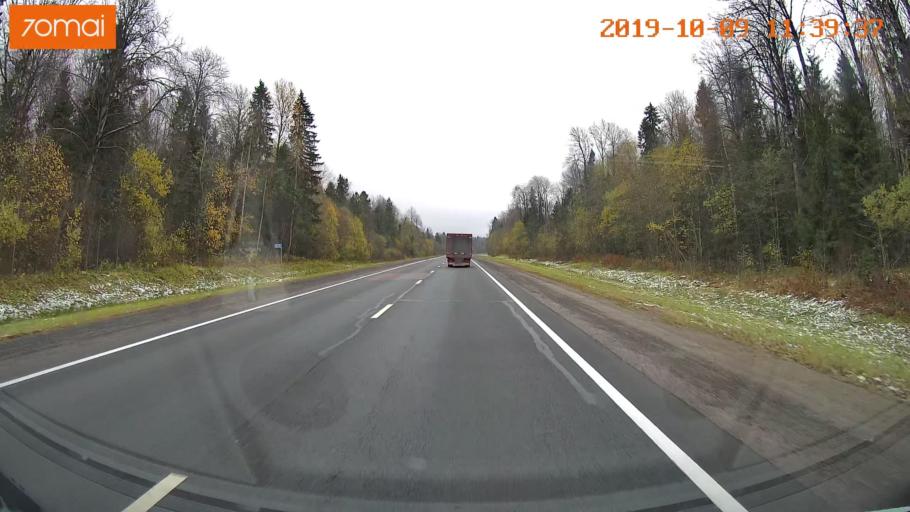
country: RU
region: Vologda
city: Gryazovets
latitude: 58.9538
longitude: 40.1678
